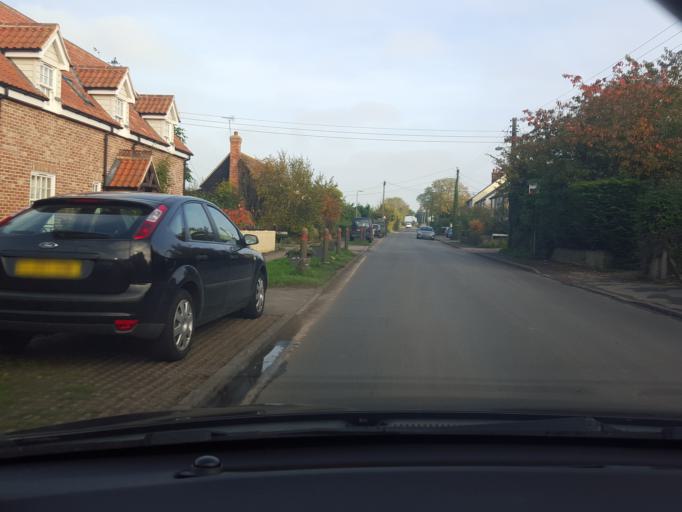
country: GB
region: England
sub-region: Essex
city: Frinton-on-Sea
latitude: 51.8516
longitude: 1.2316
